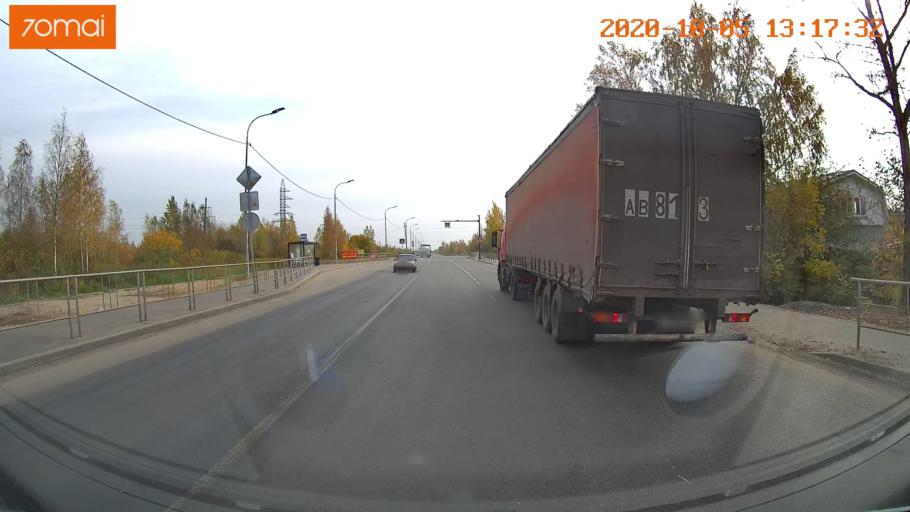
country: RU
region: Ivanovo
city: Novo-Talitsy
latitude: 56.9850
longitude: 40.9109
